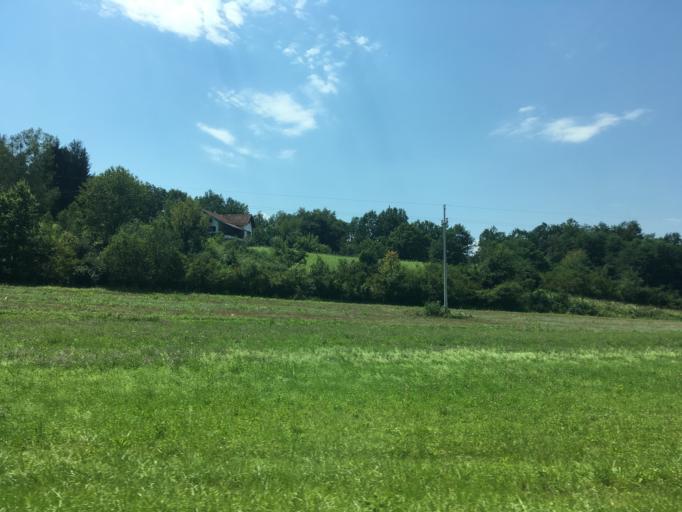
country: SI
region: Metlika
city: Metlika
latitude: 45.6103
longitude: 15.3287
